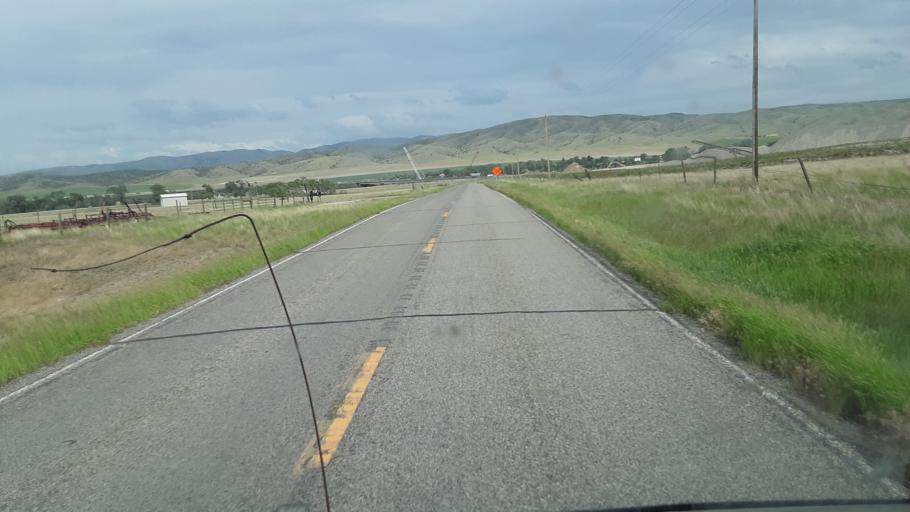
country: US
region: Montana
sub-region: Broadwater County
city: Townsend
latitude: 46.1736
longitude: -111.4577
